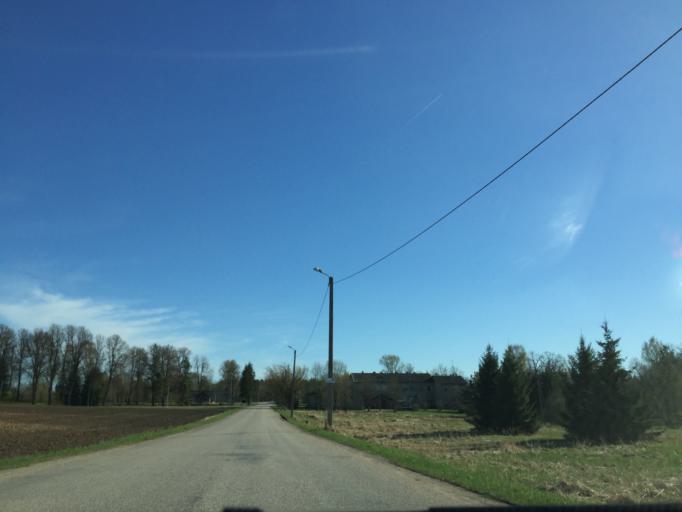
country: EE
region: Valgamaa
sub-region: Valga linn
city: Valga
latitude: 57.8706
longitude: 26.2509
